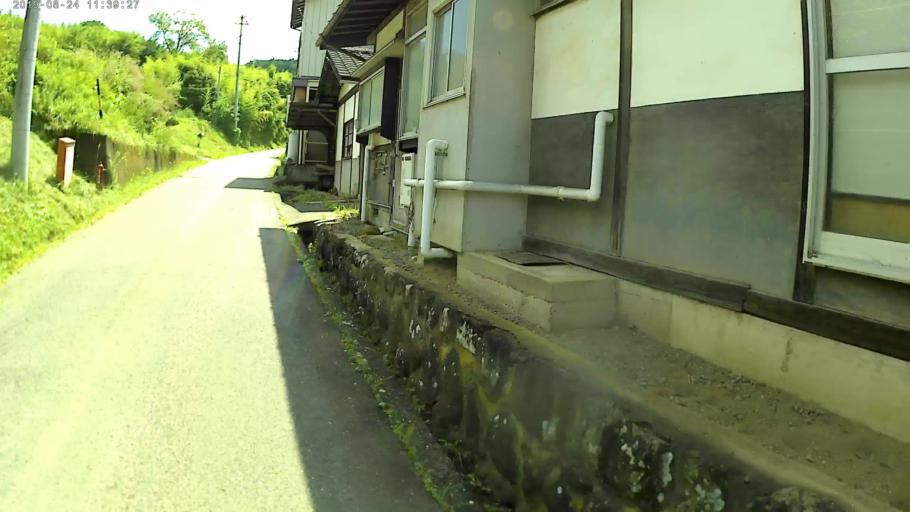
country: JP
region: Nagano
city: Kamimaruko
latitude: 36.2727
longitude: 138.3411
